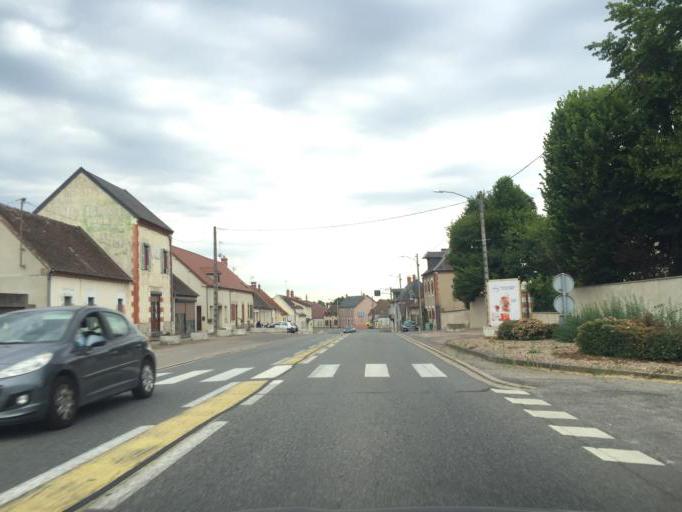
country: FR
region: Auvergne
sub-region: Departement de l'Allier
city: Bessay-sur-Allier
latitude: 46.4448
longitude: 3.3622
